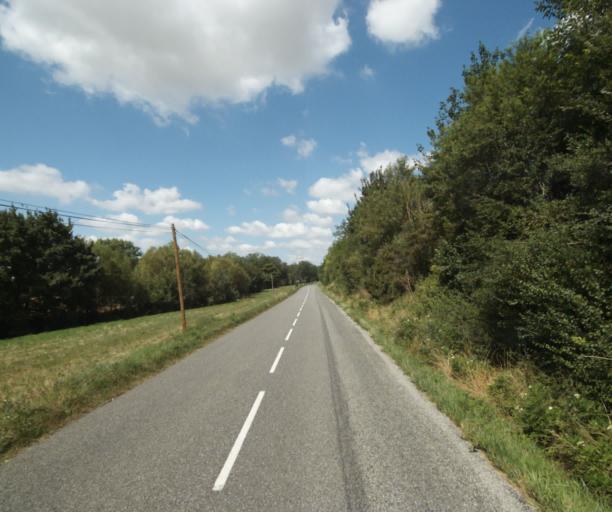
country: FR
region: Midi-Pyrenees
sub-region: Departement de la Haute-Garonne
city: Auriac-sur-Vendinelle
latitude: 43.4804
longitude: 1.7987
